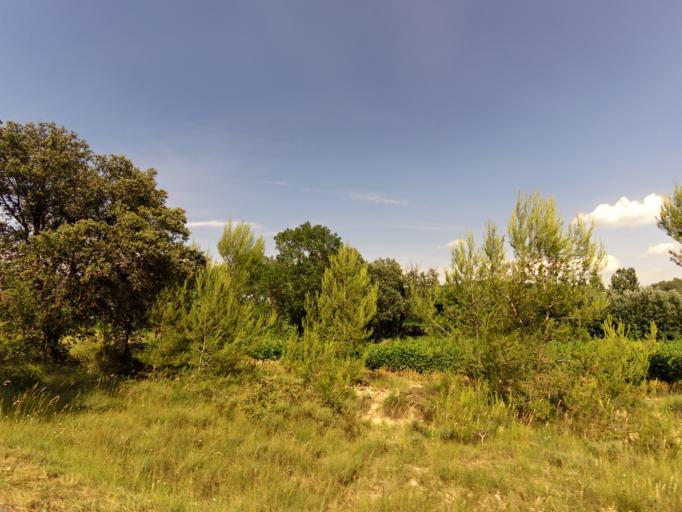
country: FR
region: Languedoc-Roussillon
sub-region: Departement du Gard
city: Quissac
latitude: 43.8596
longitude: 4.0171
